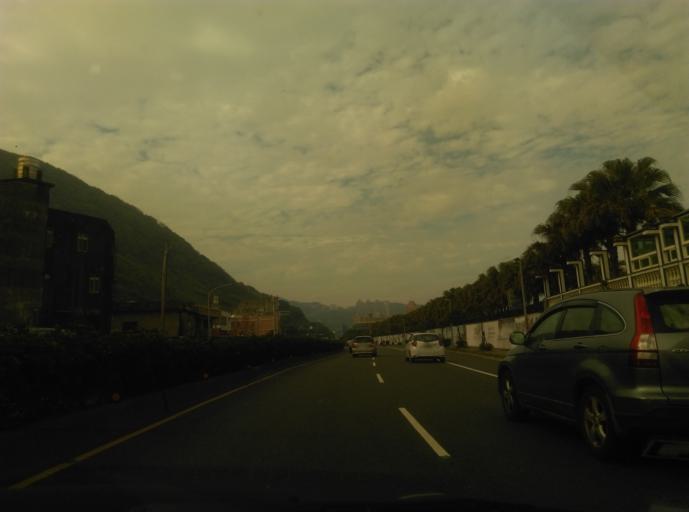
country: TW
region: Taiwan
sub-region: Keelung
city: Keelung
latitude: 25.1805
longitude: 121.6901
